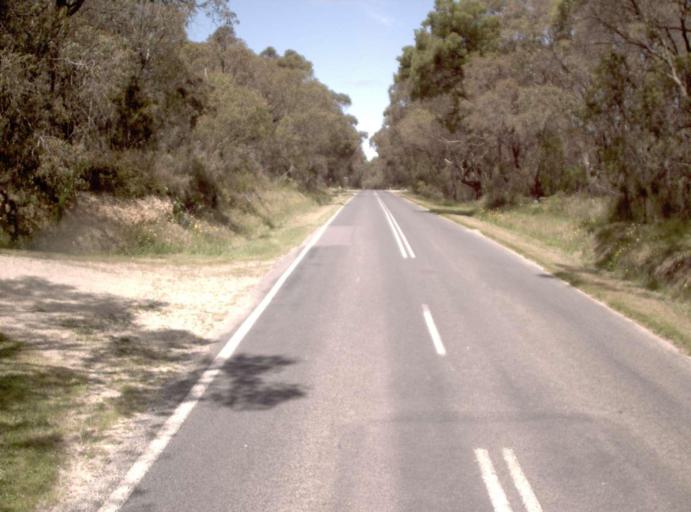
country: AU
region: Victoria
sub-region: Bass Coast
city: North Wonthaggi
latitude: -38.7360
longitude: 146.1274
